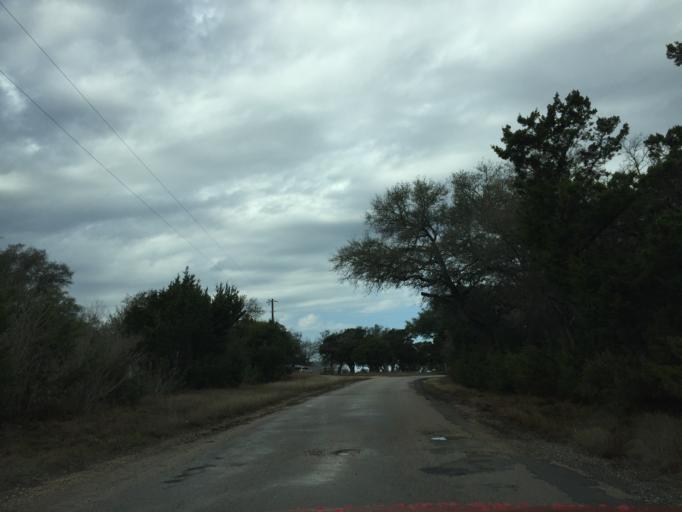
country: US
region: Texas
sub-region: Burnet County
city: Bertram
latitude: 30.6321
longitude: -98.0029
